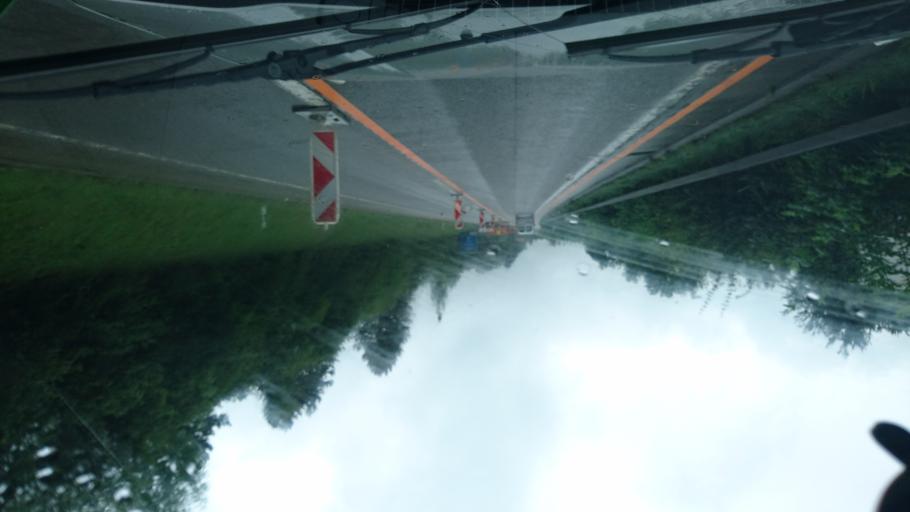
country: CH
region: Zurich
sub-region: Bezirk Hinwil
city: Durnten
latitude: 47.2721
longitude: 8.8314
